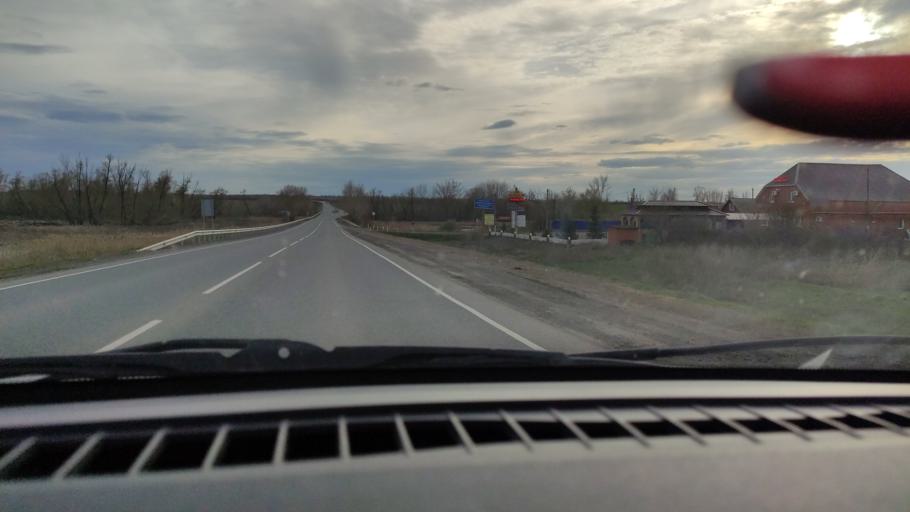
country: RU
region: Orenburg
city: Tatarskaya Kargala
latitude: 52.0242
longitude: 55.2232
